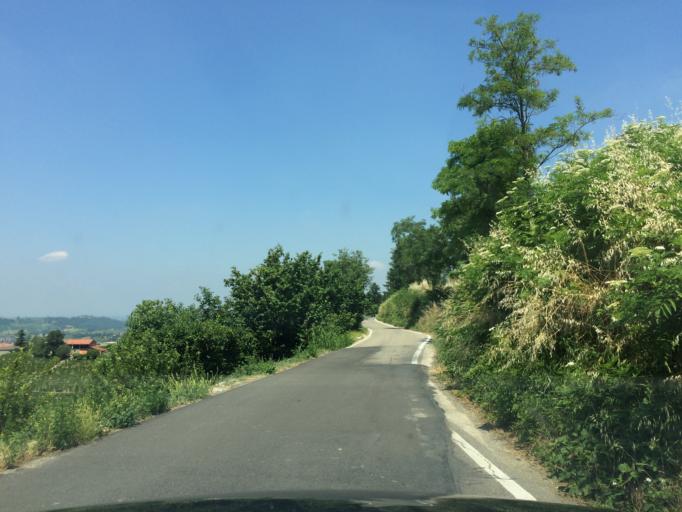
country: IT
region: Piedmont
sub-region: Provincia di Asti
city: Calosso
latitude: 44.7394
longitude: 8.2259
